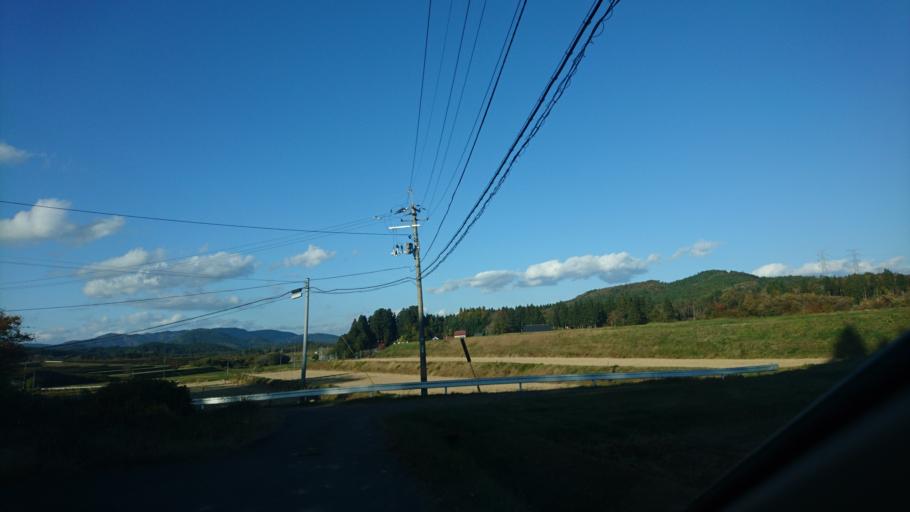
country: JP
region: Iwate
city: Ichinoseki
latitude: 38.9144
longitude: 141.2080
